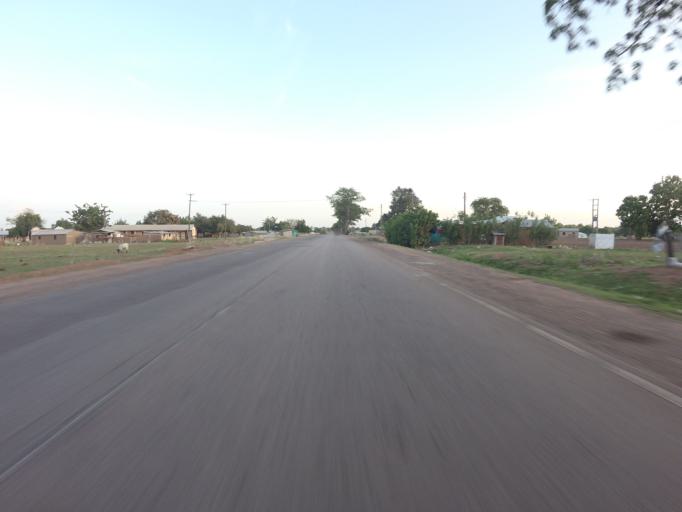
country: GH
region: Upper East
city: Navrongo
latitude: 10.9206
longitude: -1.0894
